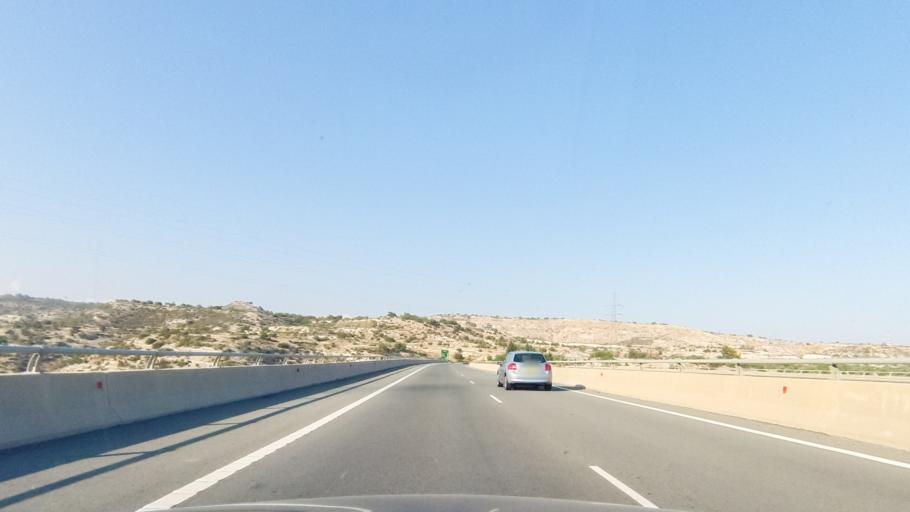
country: CY
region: Limassol
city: Sotira
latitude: 34.7021
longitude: 32.8455
